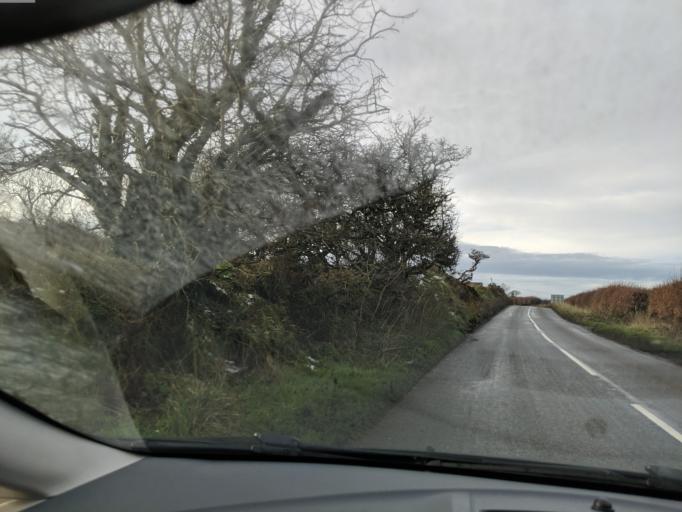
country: GB
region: England
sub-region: Cornwall
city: Jacobstow
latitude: 50.6623
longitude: -4.5790
